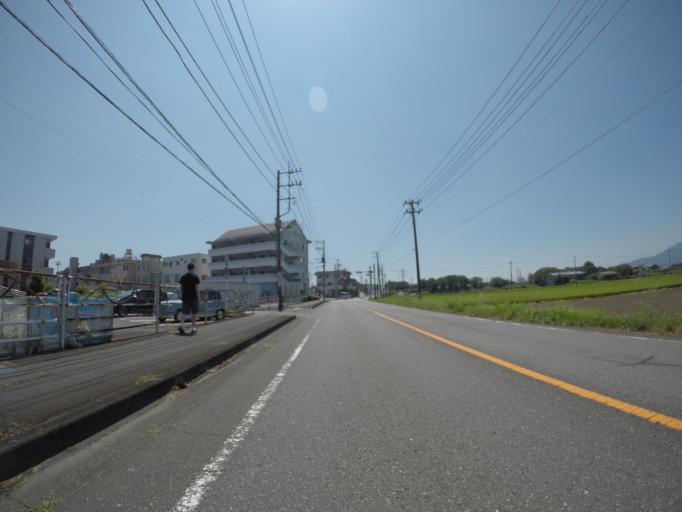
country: JP
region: Shizuoka
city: Fuji
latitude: 35.1654
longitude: 138.6662
